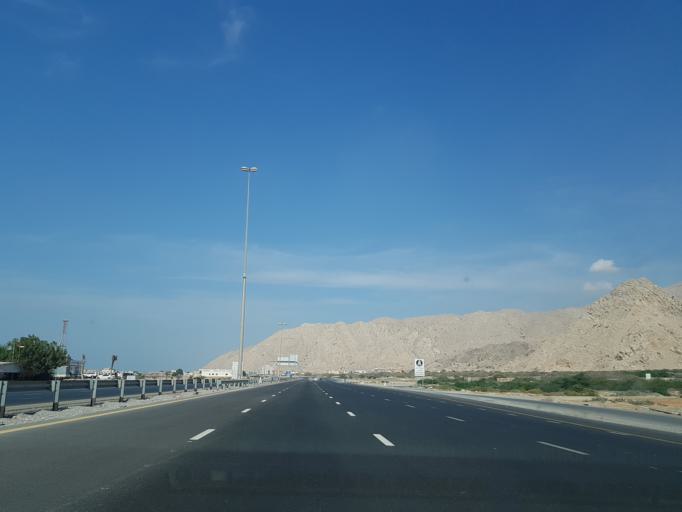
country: AE
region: Ra's al Khaymah
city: Ras al-Khaimah
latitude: 25.8394
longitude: 56.0171
